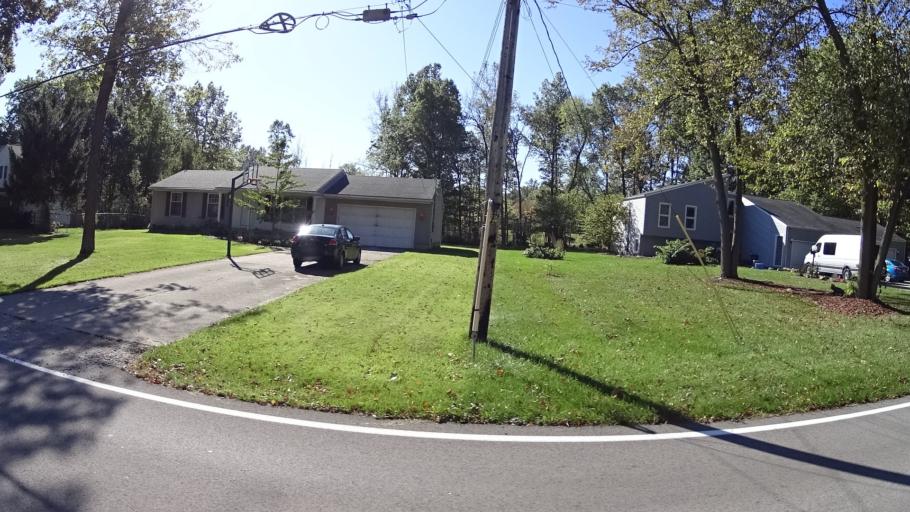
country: US
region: Ohio
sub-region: Lorain County
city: Amherst
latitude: 41.4118
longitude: -82.2482
